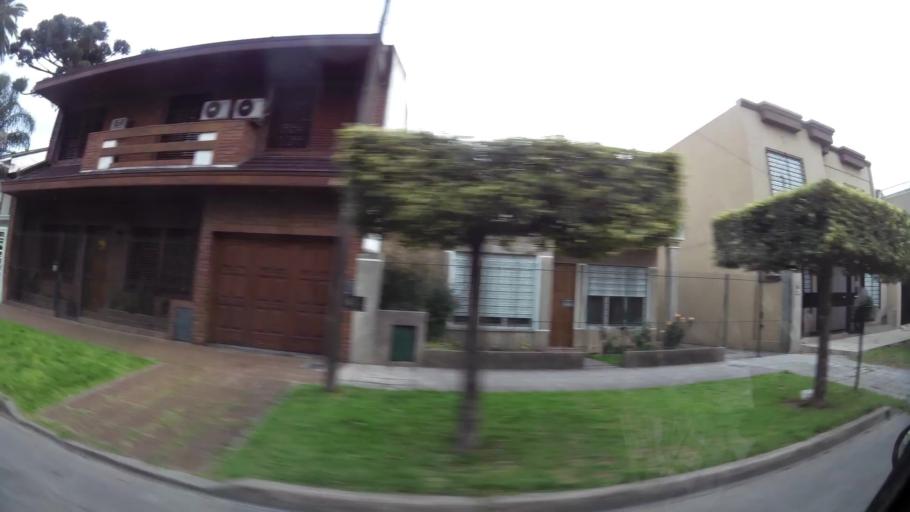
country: AR
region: Buenos Aires
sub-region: Partido de Quilmes
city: Quilmes
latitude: -34.7371
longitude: -58.2458
